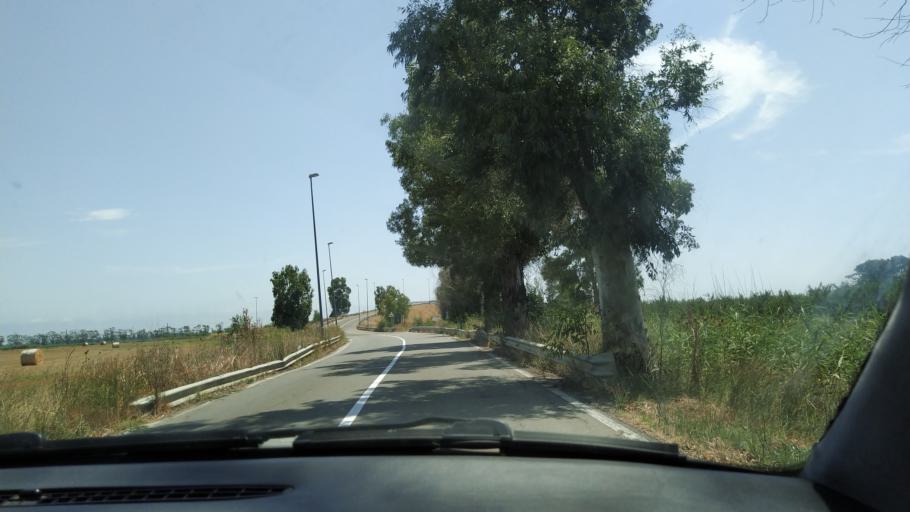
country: IT
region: Basilicate
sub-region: Provincia di Matera
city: Marconia
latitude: 40.3367
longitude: 16.7718
